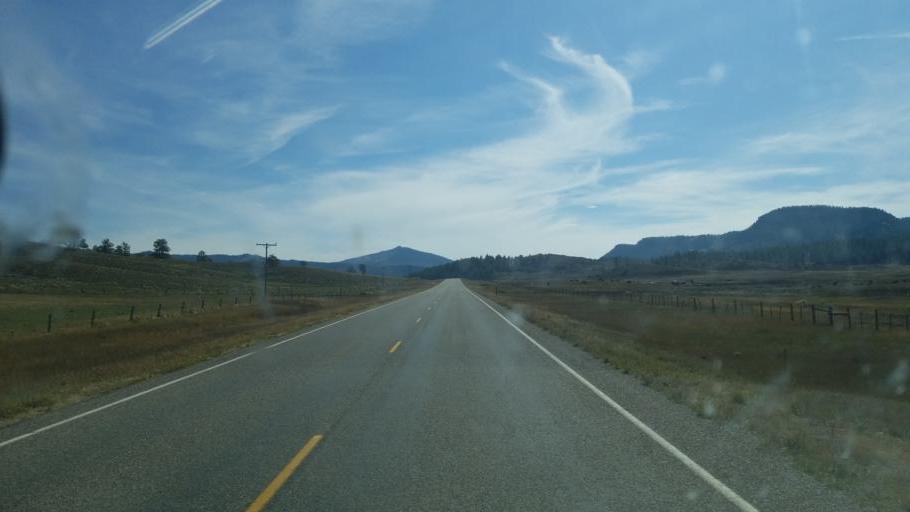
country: US
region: New Mexico
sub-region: Rio Arriba County
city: Dulce
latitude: 37.0269
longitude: -106.8240
